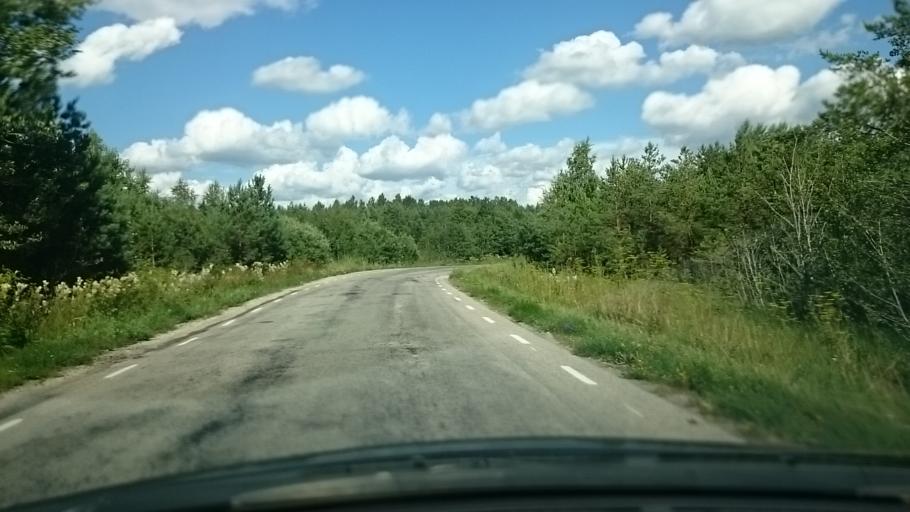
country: EE
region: Laeaene
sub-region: Haapsalu linn
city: Haapsalu
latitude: 59.0570
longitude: 23.5412
